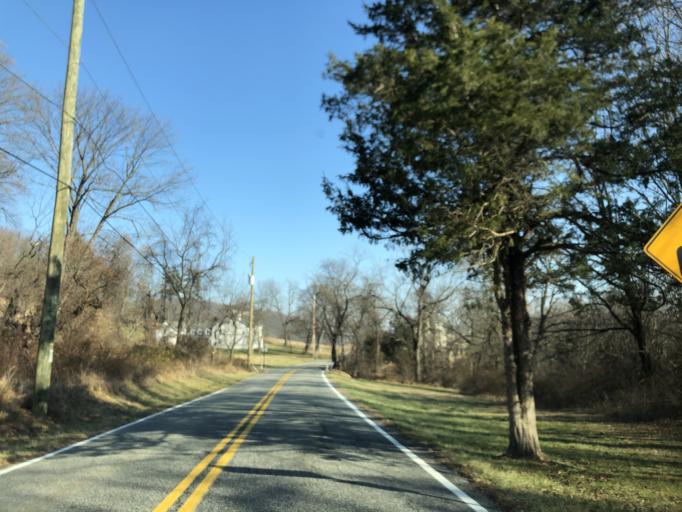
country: US
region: Pennsylvania
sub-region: Chester County
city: Chesterbrook
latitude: 40.0836
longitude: -75.4642
